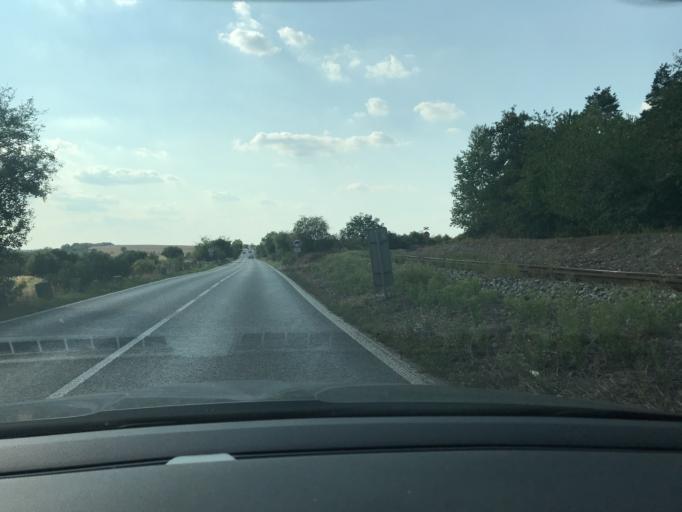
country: CZ
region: Central Bohemia
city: Kralupy nad Vltavou
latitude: 50.2325
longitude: 14.2761
